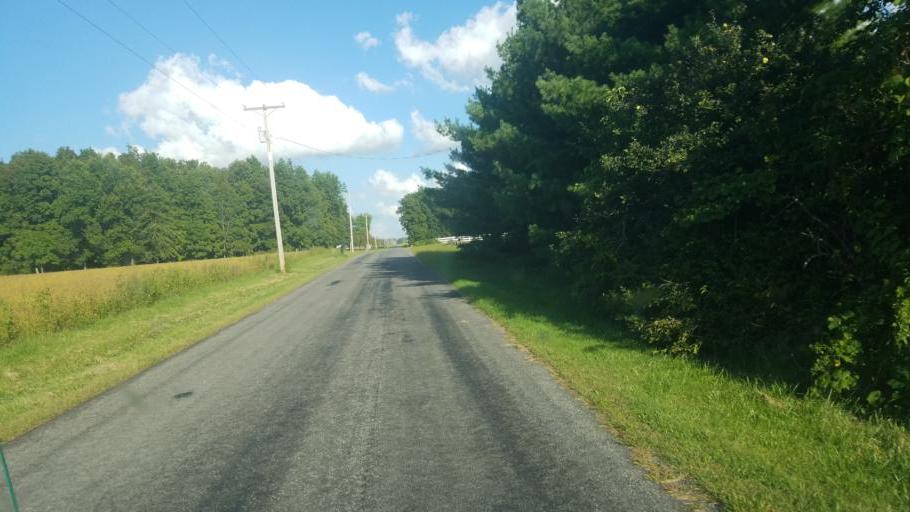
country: US
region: Ohio
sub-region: Hancock County
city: Arlington
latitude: 40.9362
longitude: -83.7154
